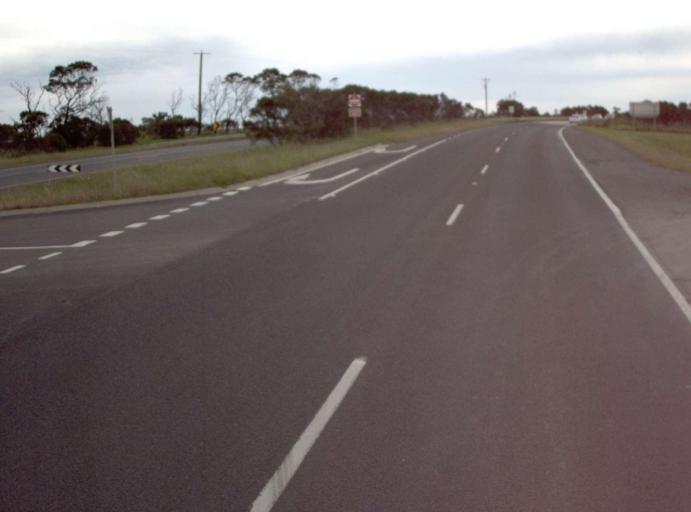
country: AU
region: Victoria
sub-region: Cardinia
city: Koo-Wee-Rup
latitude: -38.2134
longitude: 145.4594
